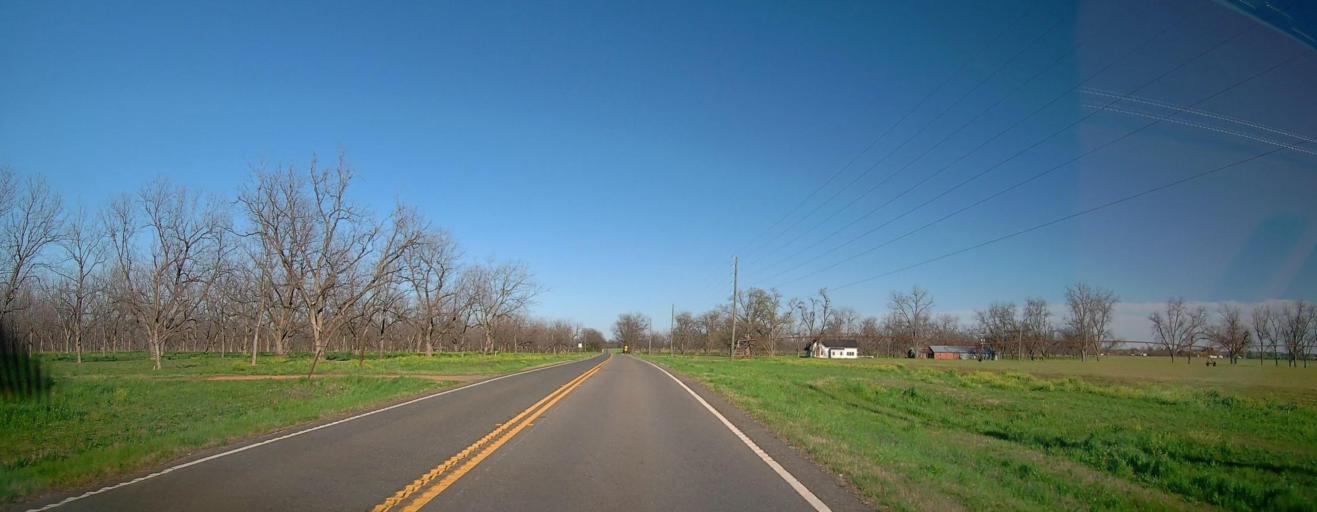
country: US
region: Georgia
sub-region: Houston County
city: Perry
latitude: 32.4392
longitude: -83.8227
